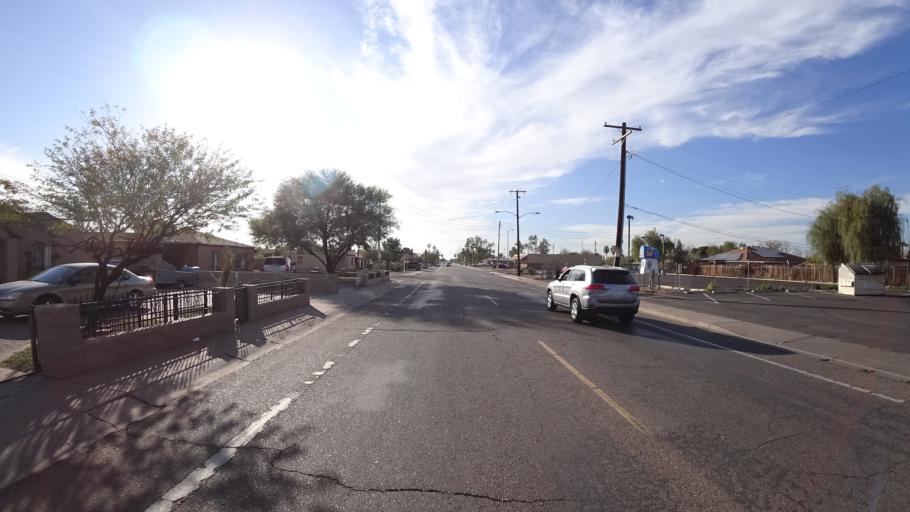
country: US
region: Arizona
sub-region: Maricopa County
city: Phoenix
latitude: 33.4587
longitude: -112.1278
